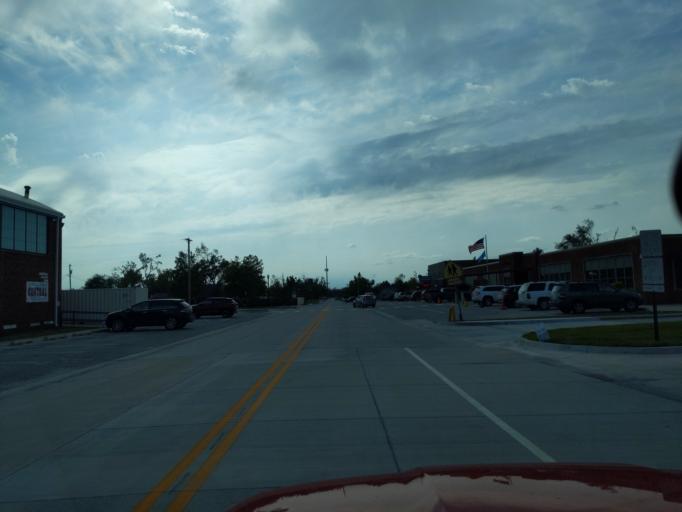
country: US
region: Oklahoma
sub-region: Cleveland County
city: Moore
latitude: 35.3405
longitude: -97.4874
